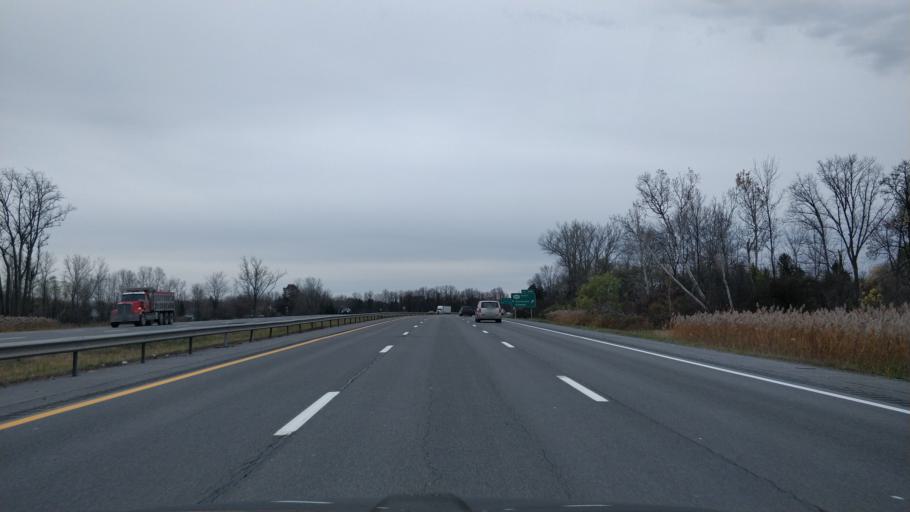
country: US
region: New York
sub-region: Onondaga County
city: North Syracuse
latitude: 43.1489
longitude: -76.1102
